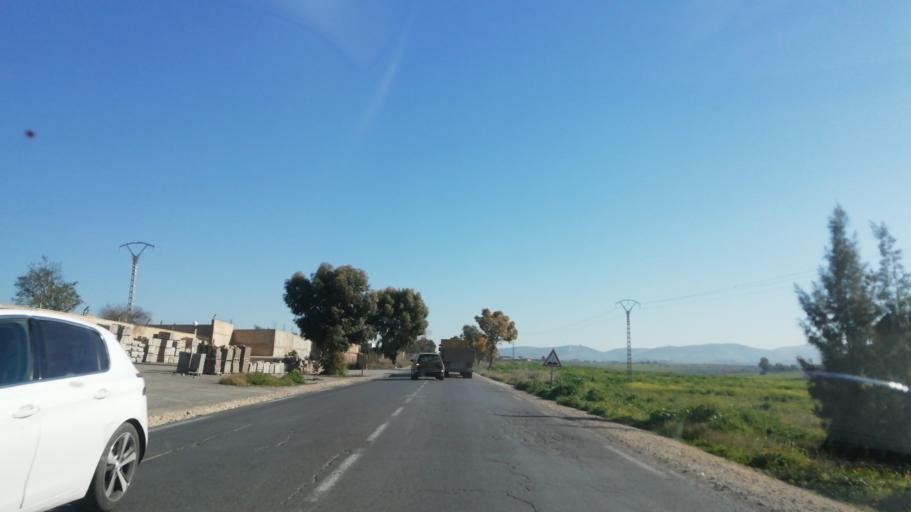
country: DZ
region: Relizane
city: Zemoura
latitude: 35.7537
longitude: 0.6823
